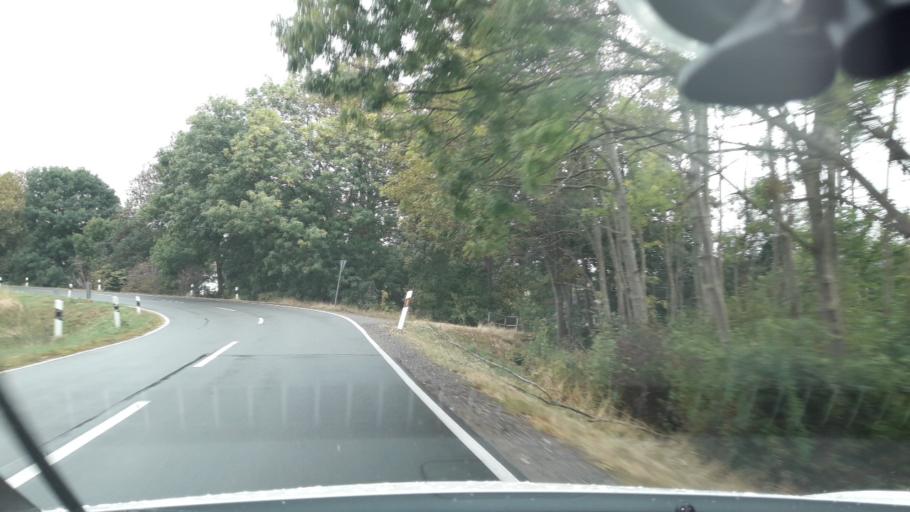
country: DE
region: Lower Saxony
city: Gielde
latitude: 51.9765
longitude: 10.4914
